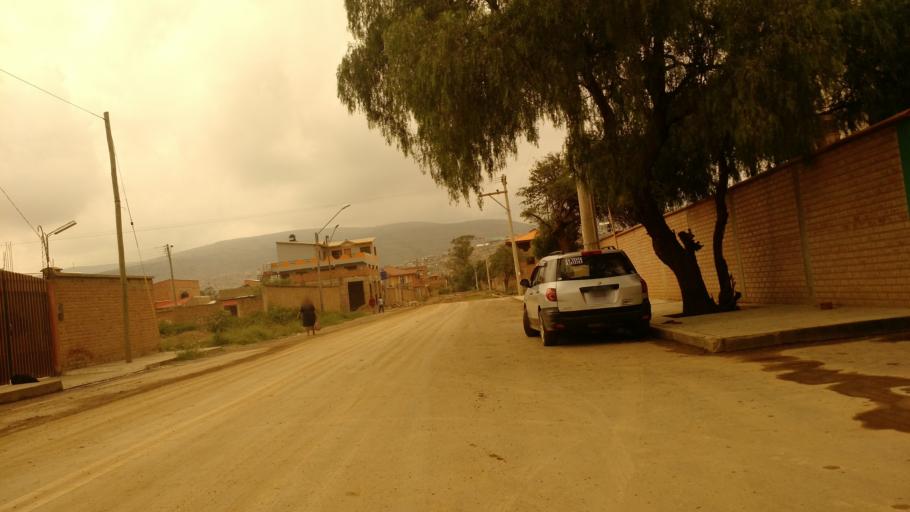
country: BO
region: Cochabamba
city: Cochabamba
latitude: -17.4503
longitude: -66.1499
